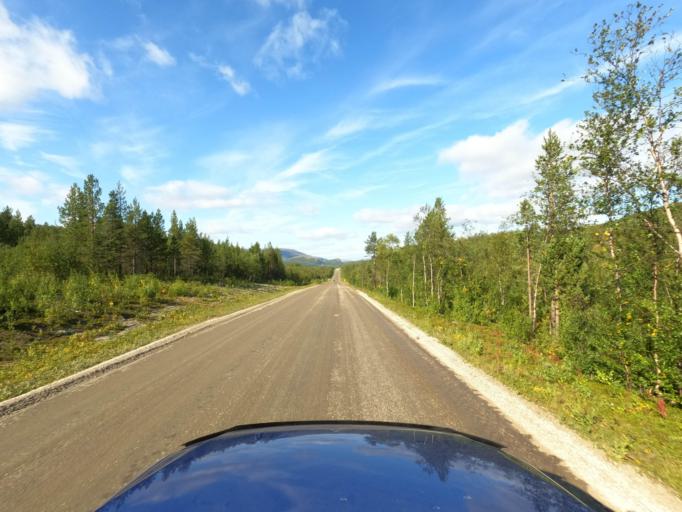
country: NO
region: Finnmark Fylke
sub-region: Porsanger
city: Lakselv
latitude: 69.8739
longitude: 25.0340
